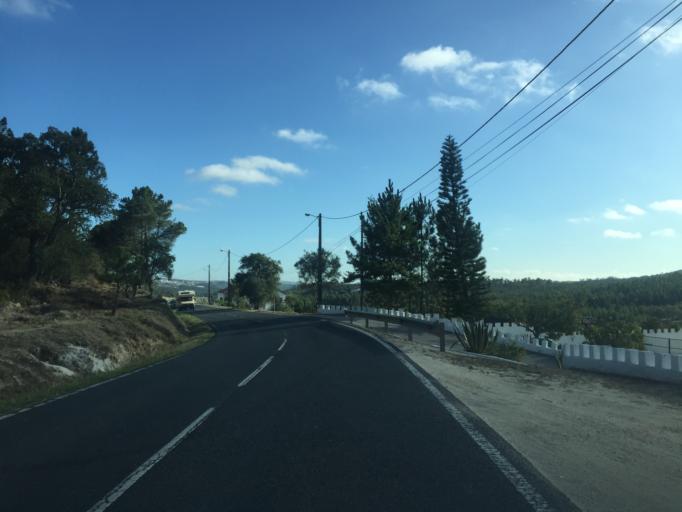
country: PT
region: Lisbon
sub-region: Torres Vedras
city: Torres Vedras
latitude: 39.1310
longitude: -9.2630
